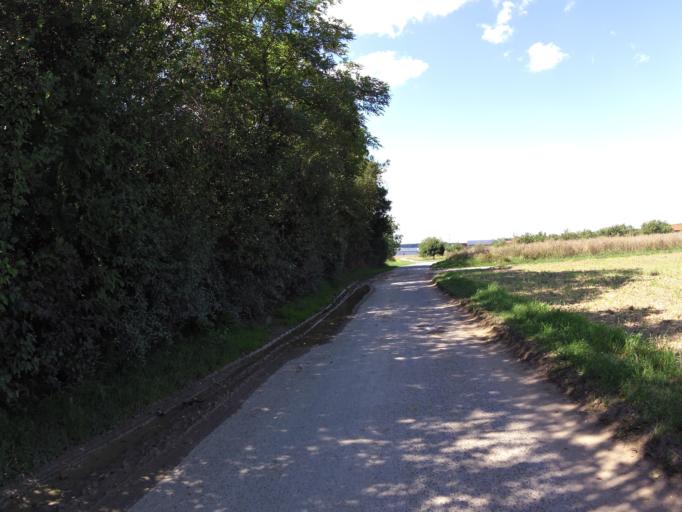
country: DE
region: Bavaria
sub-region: Regierungsbezirk Unterfranken
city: Segnitz
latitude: 49.6841
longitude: 10.1502
